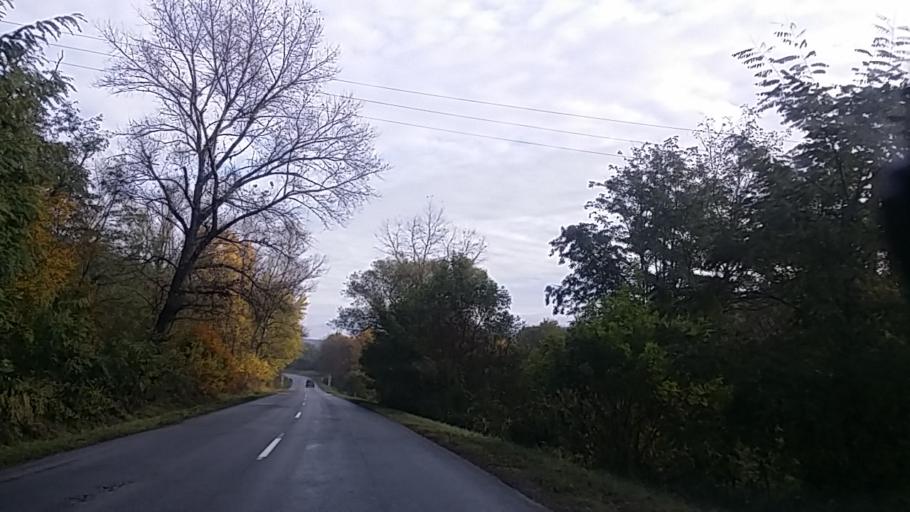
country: HU
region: Heves
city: Szilvasvarad
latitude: 48.0918
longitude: 20.3795
